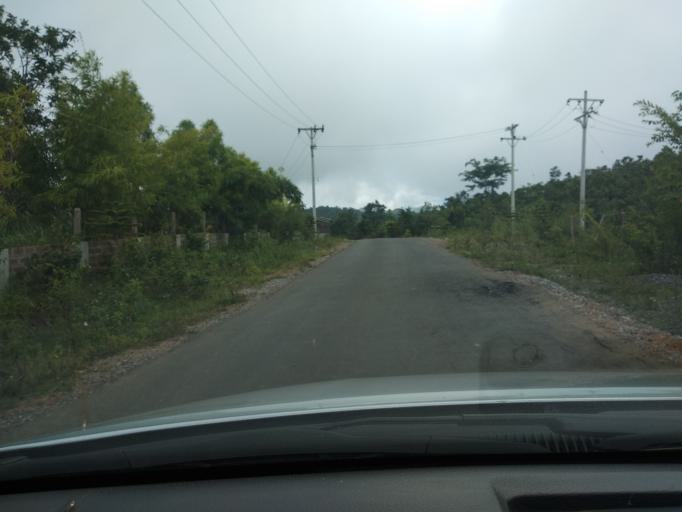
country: MM
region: Mandalay
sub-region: Pyin Oo Lwin District
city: Pyin Oo Lwin
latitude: 21.9213
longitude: 96.3781
